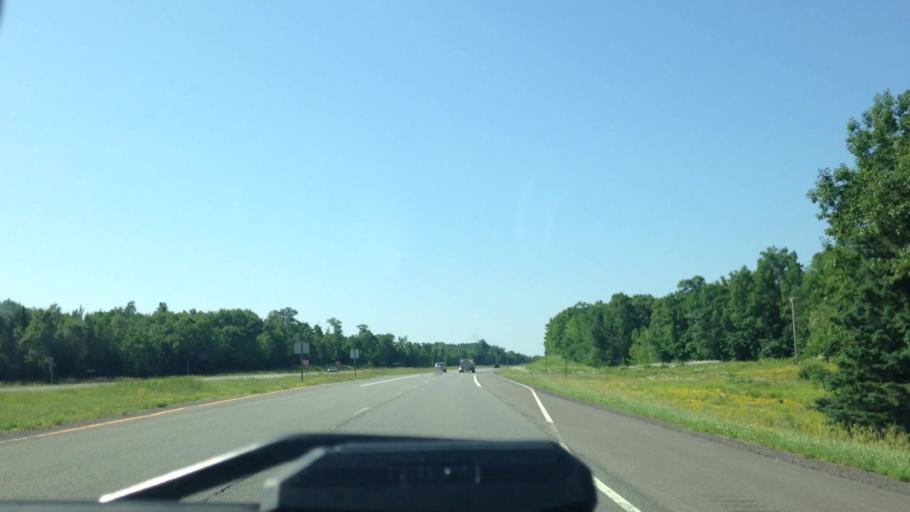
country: US
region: Wisconsin
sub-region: Douglas County
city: Lake Nebagamon
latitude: 46.4184
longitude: -91.8099
